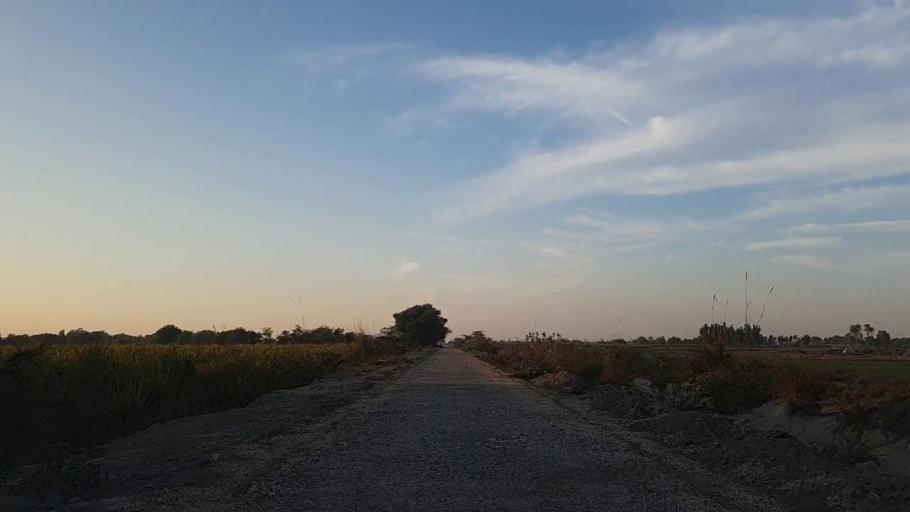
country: PK
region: Sindh
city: Bandhi
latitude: 26.6158
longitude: 68.3545
